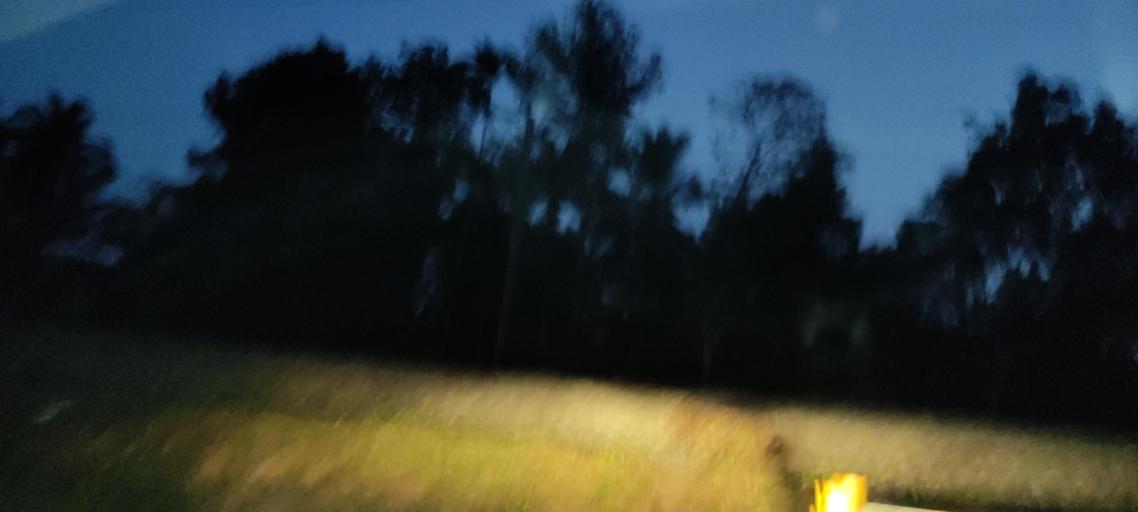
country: IN
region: Kerala
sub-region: Alappuzha
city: Mavelikara
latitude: 9.3203
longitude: 76.4275
